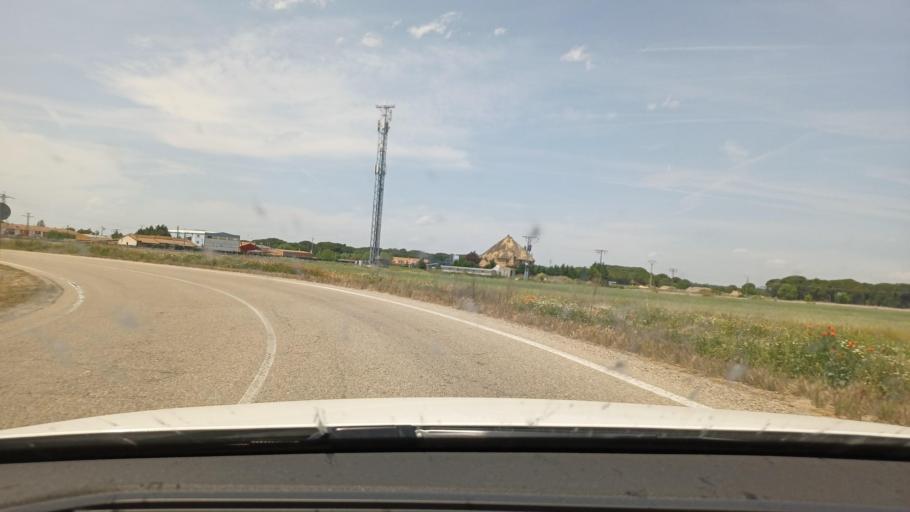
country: ES
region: Castille and Leon
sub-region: Provincia de Valladolid
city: Aldeamayor de San Martin
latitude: 41.5140
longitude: -4.6314
